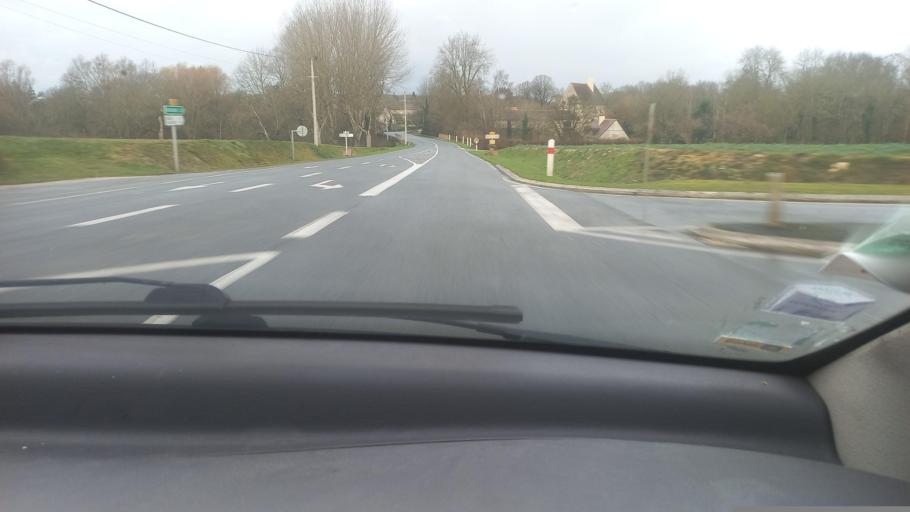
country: FR
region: Centre
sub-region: Departement de l'Indre
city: Neuvy-Pailloux
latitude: 46.8203
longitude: 1.9303
